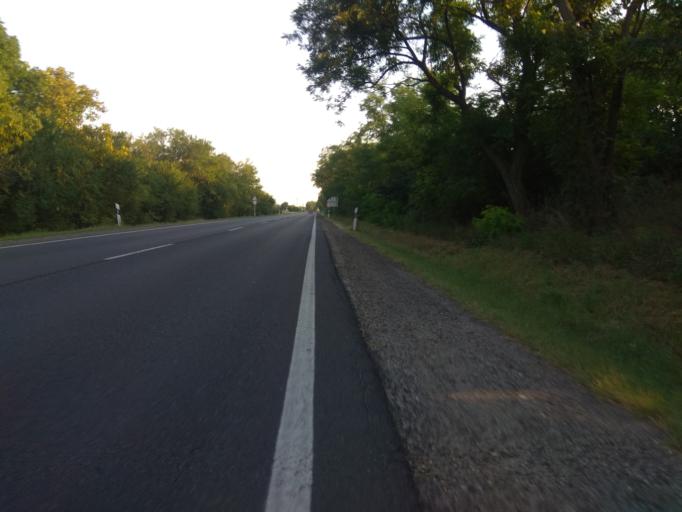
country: HU
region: Borsod-Abauj-Zemplen
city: Emod
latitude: 47.9532
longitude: 20.8336
